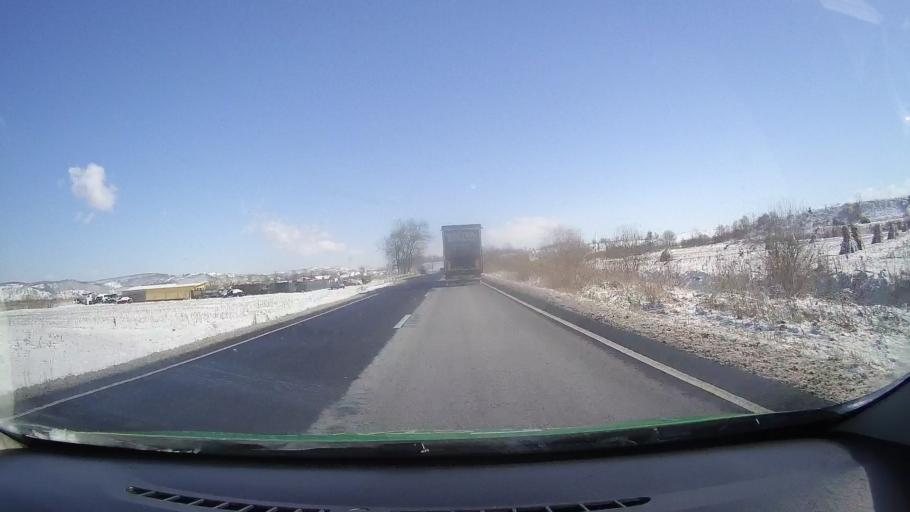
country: RO
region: Sibiu
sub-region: Comuna Porumbacu de Jos
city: Porumbacu de Jos
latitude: 45.7560
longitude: 24.4414
